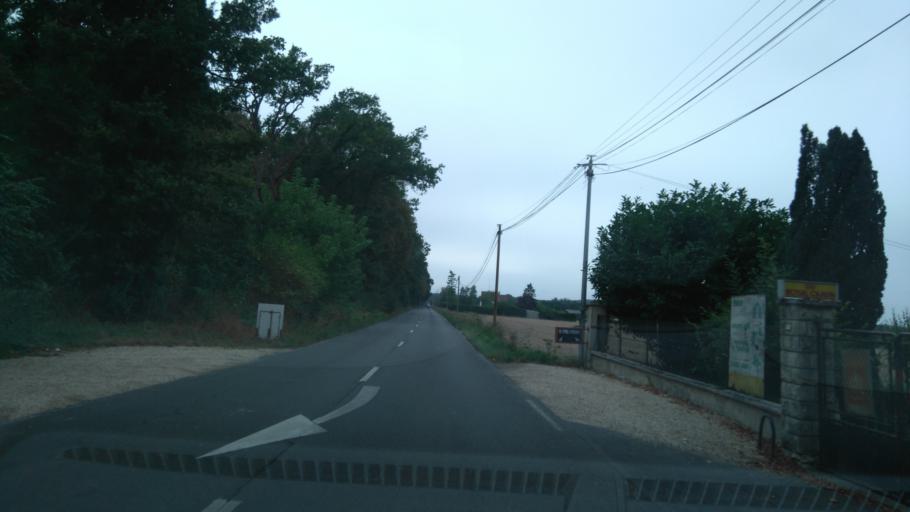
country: FR
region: Picardie
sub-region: Departement de l'Oise
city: Gouvieux
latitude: 49.1879
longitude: 2.4013
